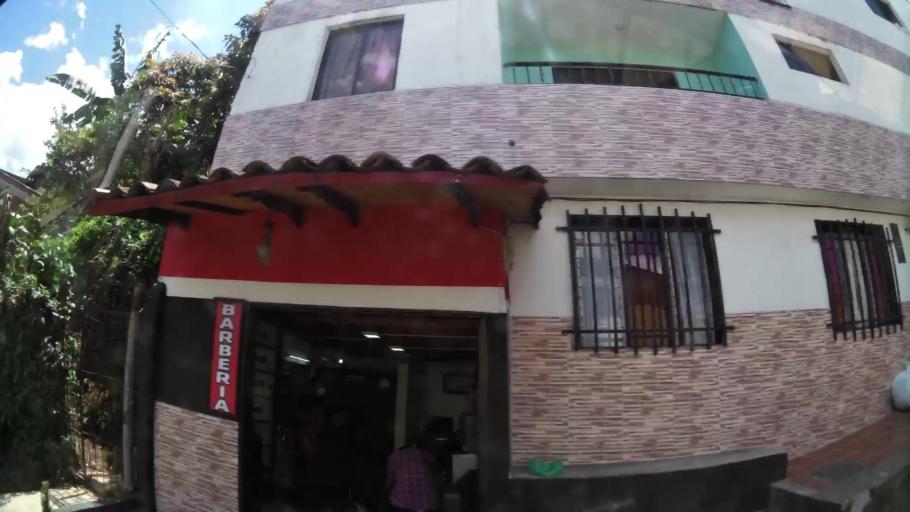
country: CO
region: Antioquia
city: La Estrella
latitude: 6.1532
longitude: -75.6388
